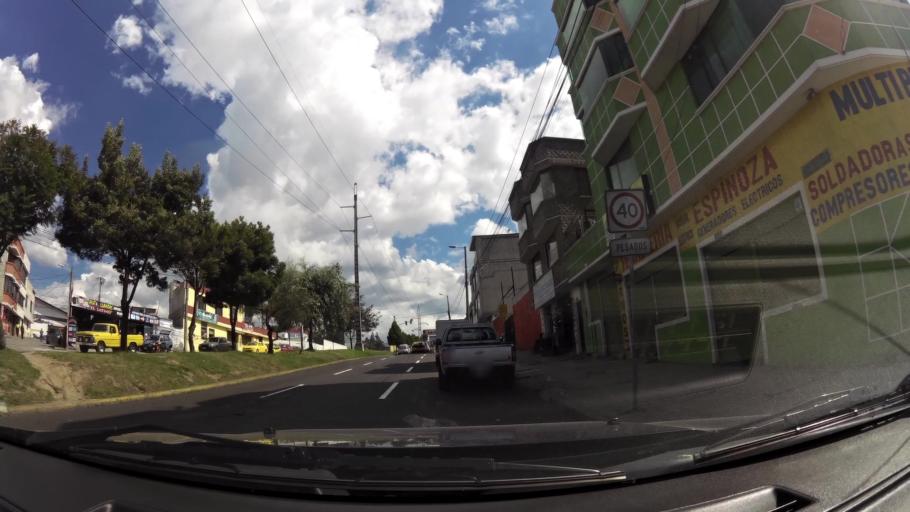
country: EC
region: Pichincha
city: Quito
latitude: -0.1032
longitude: -78.4699
